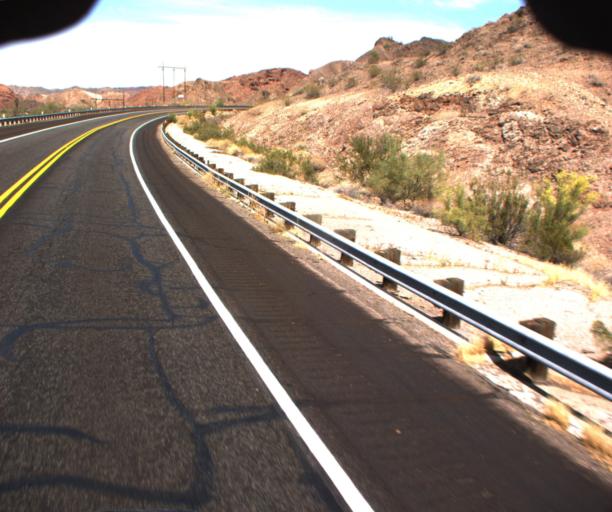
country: US
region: Arizona
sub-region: La Paz County
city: Cienega Springs
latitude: 34.2384
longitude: -114.1764
